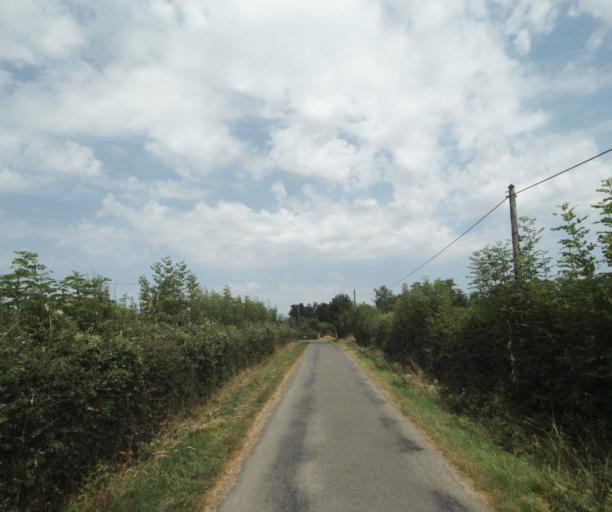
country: FR
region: Bourgogne
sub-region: Departement de Saone-et-Loire
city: Gueugnon
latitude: 46.5905
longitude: 4.0411
